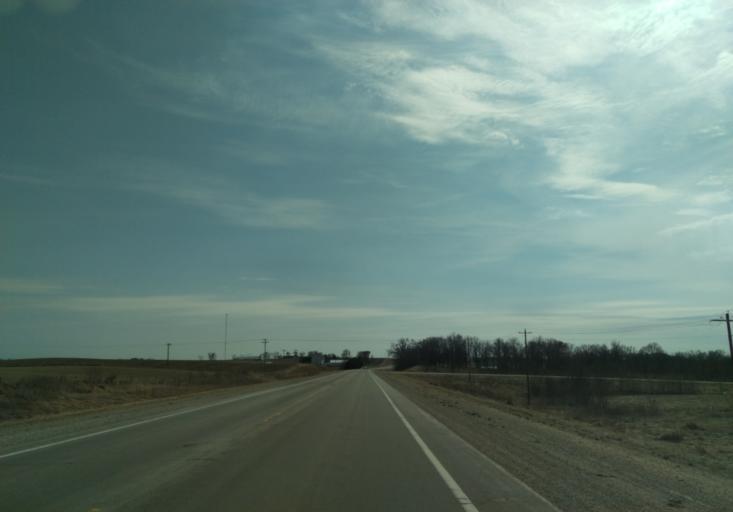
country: US
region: Iowa
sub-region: Winneshiek County
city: Decorah
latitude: 43.4306
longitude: -91.8599
